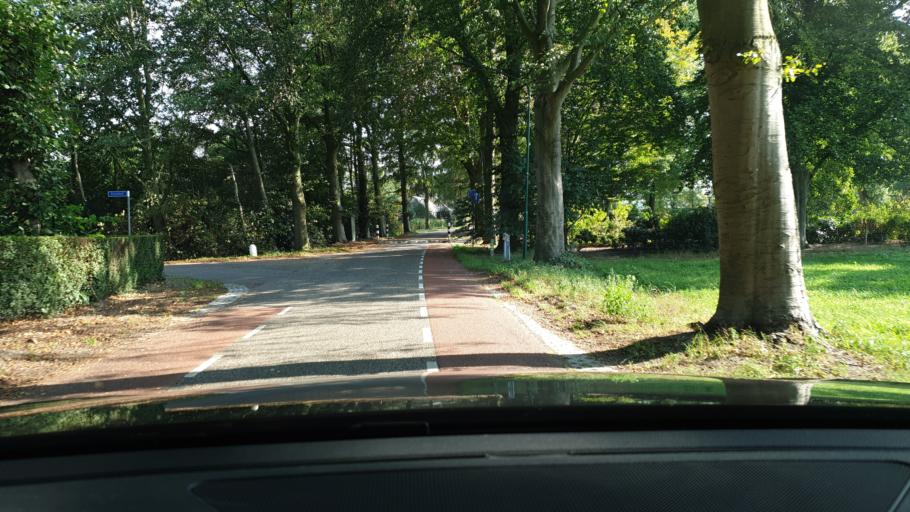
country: NL
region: North Brabant
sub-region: Gemeente Bernheze
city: Heesch
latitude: 51.7142
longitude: 5.5506
